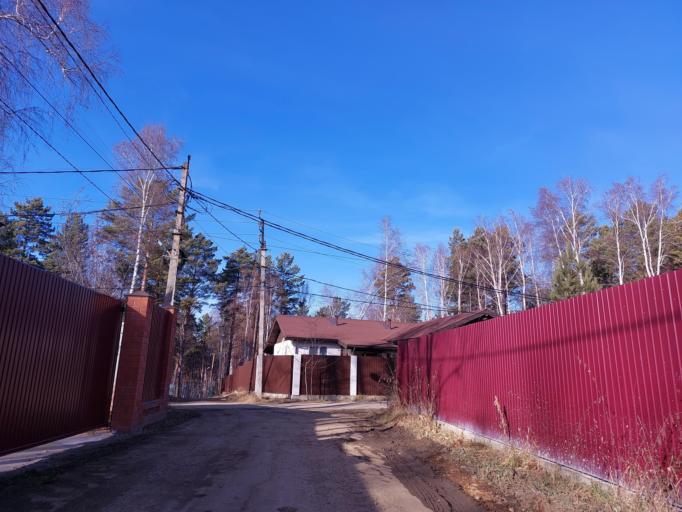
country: RU
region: Irkutsk
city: Pivovarikha
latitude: 52.1874
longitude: 104.4545
